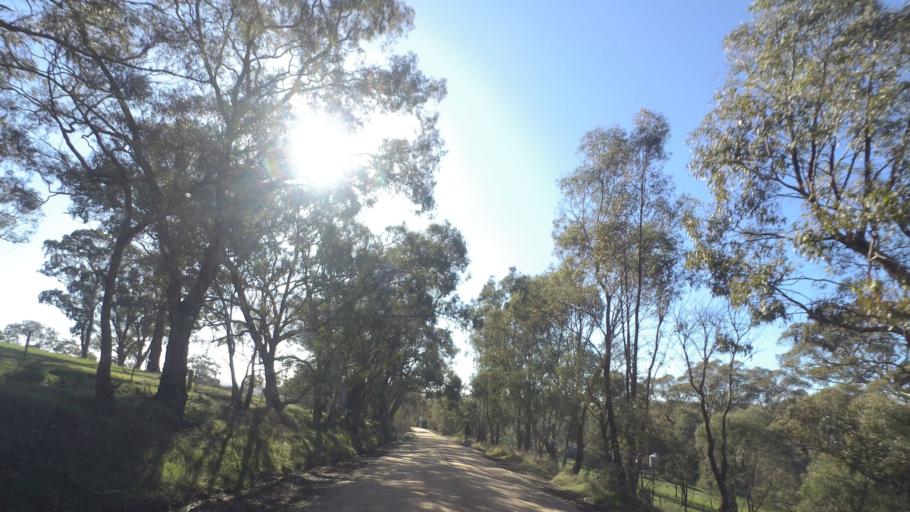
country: AU
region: Victoria
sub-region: Mount Alexander
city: Castlemaine
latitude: -37.1195
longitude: 144.4145
